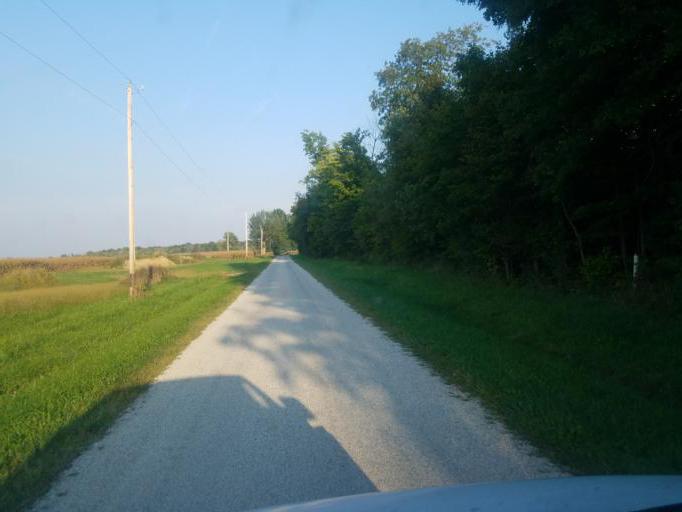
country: US
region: Ohio
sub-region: Crawford County
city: Bucyrus
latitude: 40.9069
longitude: -82.9044
